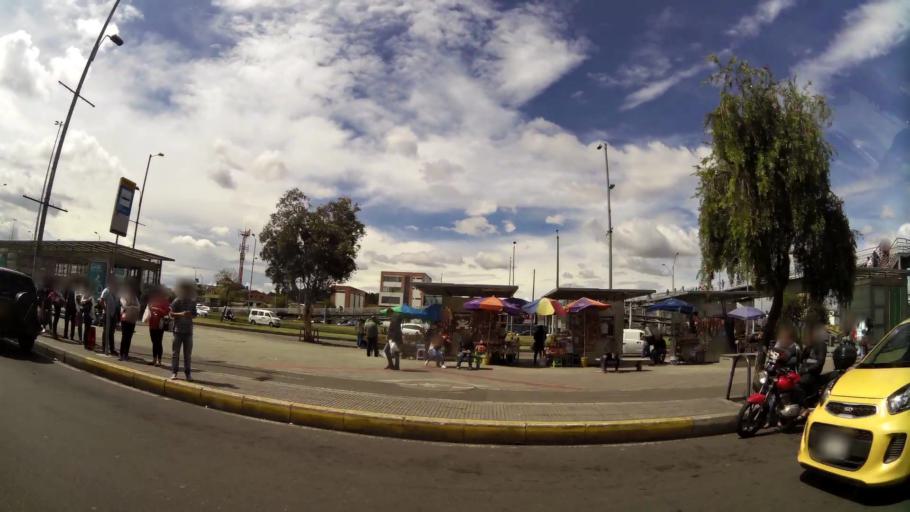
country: CO
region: Bogota D.C.
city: Bogota
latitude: 4.6297
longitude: -74.1360
